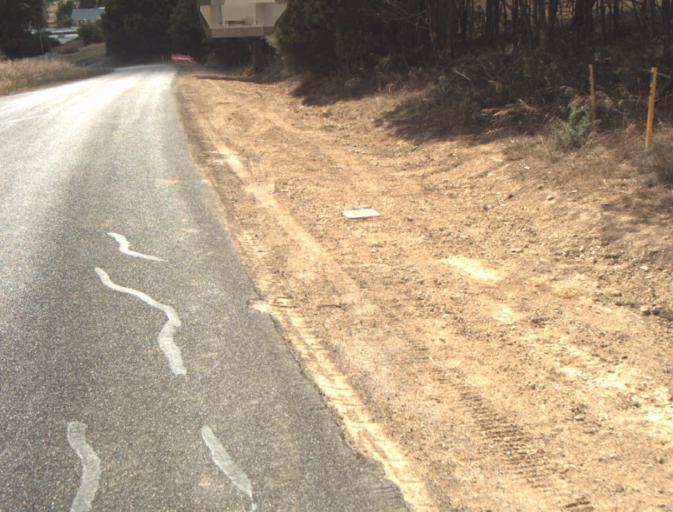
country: AU
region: Tasmania
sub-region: Launceston
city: Mayfield
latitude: -41.2565
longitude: 147.2103
